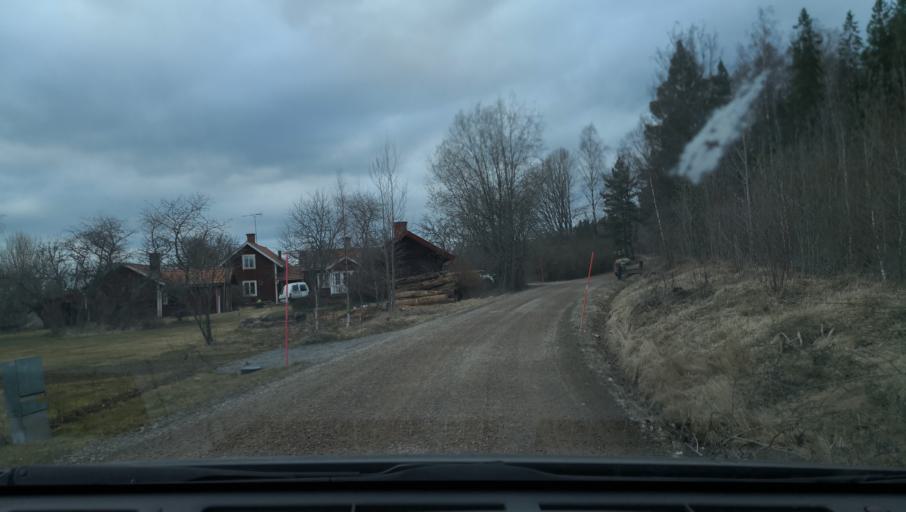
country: SE
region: Vaestmanland
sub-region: Kopings Kommun
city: Koping
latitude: 59.5302
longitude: 15.9051
